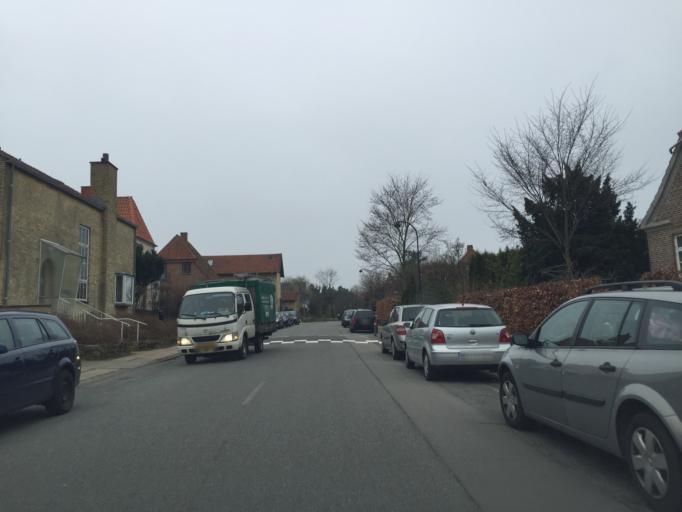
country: DK
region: Capital Region
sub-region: Gentofte Kommune
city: Charlottenlund
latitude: 55.7414
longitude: 12.5462
